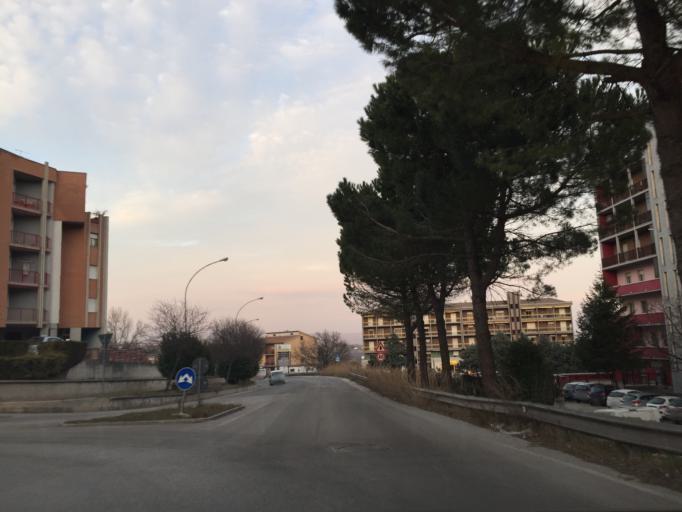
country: IT
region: Molise
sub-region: Provincia di Campobasso
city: Campobasso
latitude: 41.5601
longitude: 14.6811
